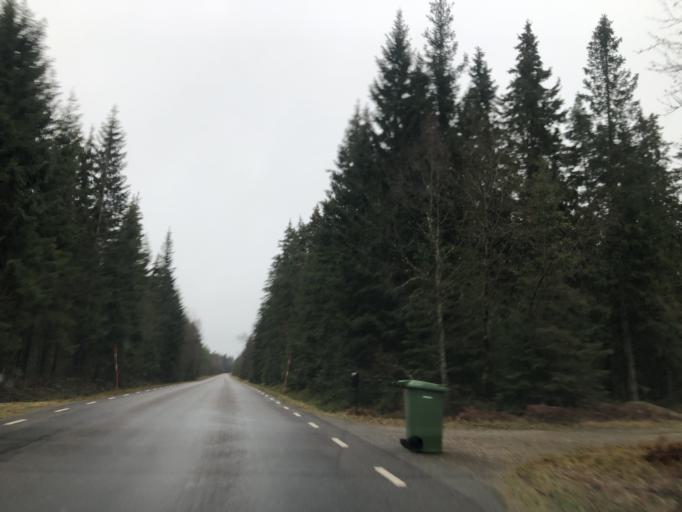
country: SE
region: Vaestra Goetaland
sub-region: Ulricehamns Kommun
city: Ulricehamn
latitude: 57.7576
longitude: 13.4988
